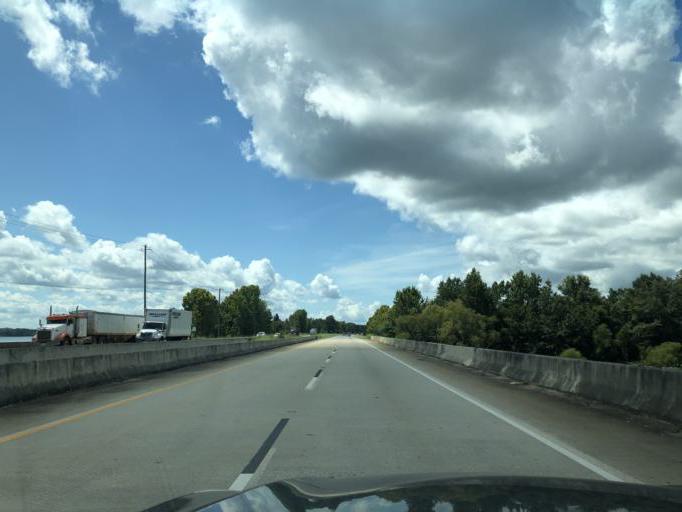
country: US
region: Alabama
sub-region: Barbour County
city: Eufaula
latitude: 31.9832
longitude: -85.1145
